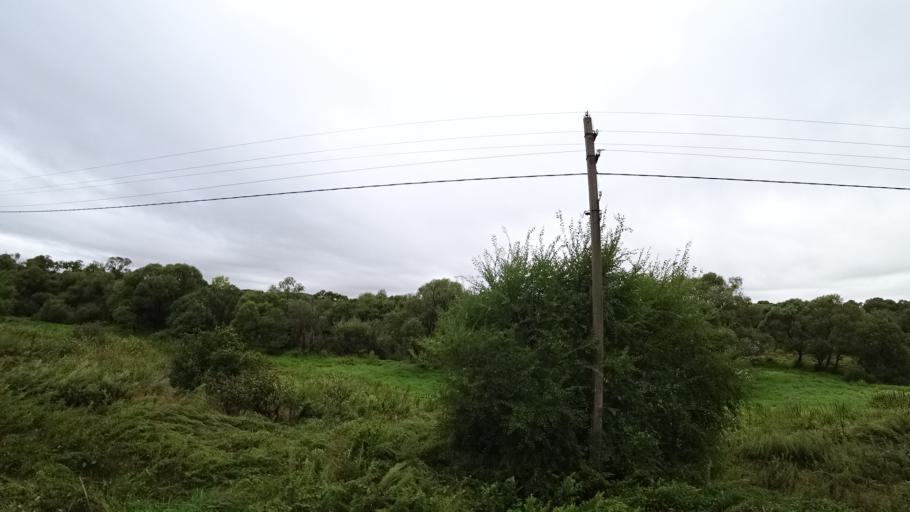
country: RU
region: Primorskiy
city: Monastyrishche
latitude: 44.2693
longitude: 132.4040
